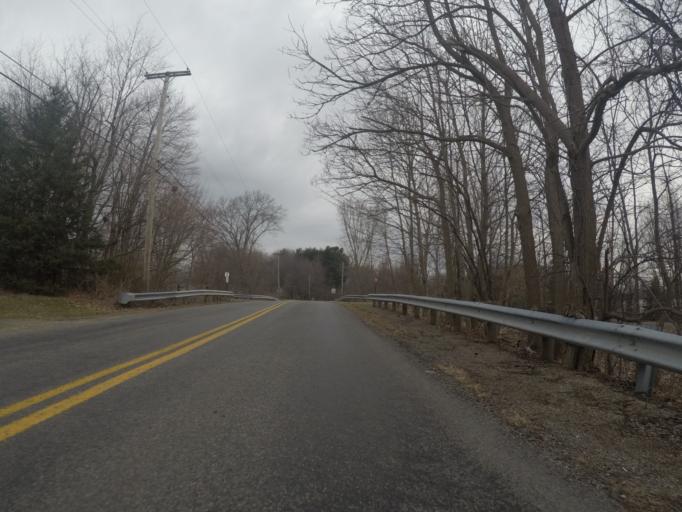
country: US
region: Ohio
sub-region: Portage County
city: Ravenna
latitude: 41.1688
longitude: -81.2850
